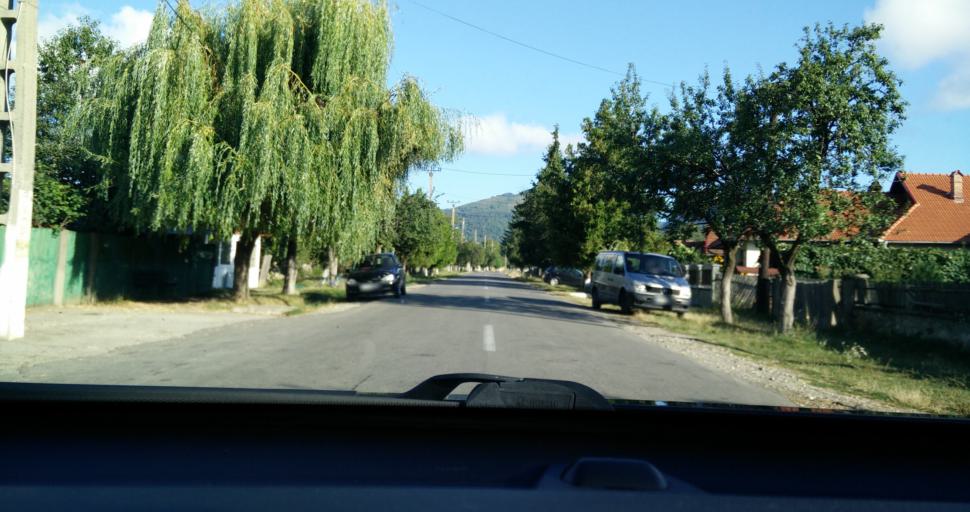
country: RO
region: Gorj
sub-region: Comuna Polovragi
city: Polovragi
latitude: 45.1733
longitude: 23.8019
